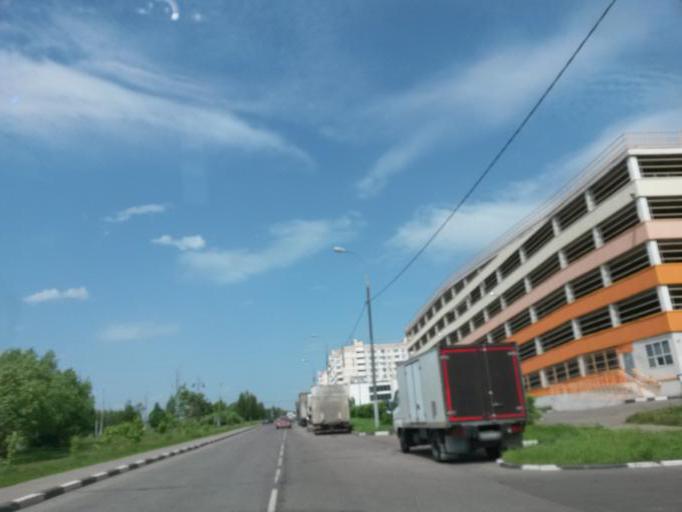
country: RU
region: Moskovskaya
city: Kommunarka
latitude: 55.5407
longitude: 37.5153
